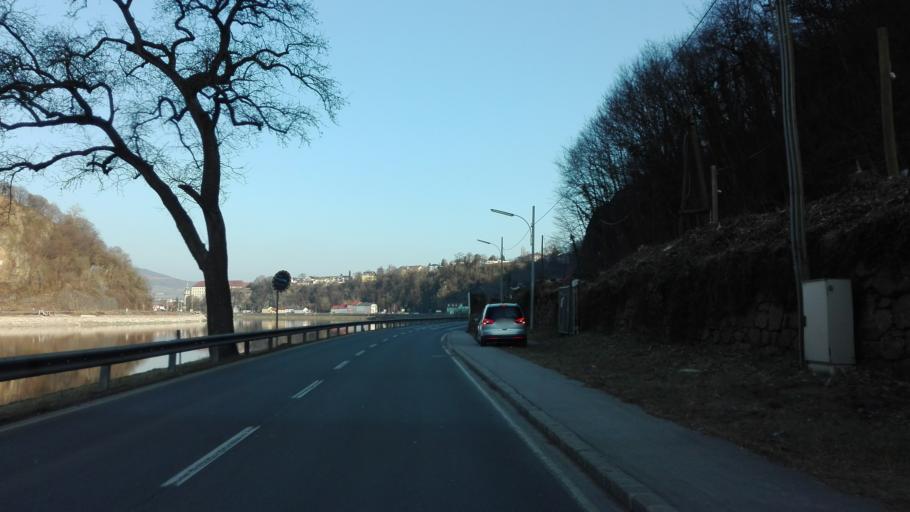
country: AT
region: Upper Austria
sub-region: Linz Stadt
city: Linz
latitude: 48.3063
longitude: 14.2632
